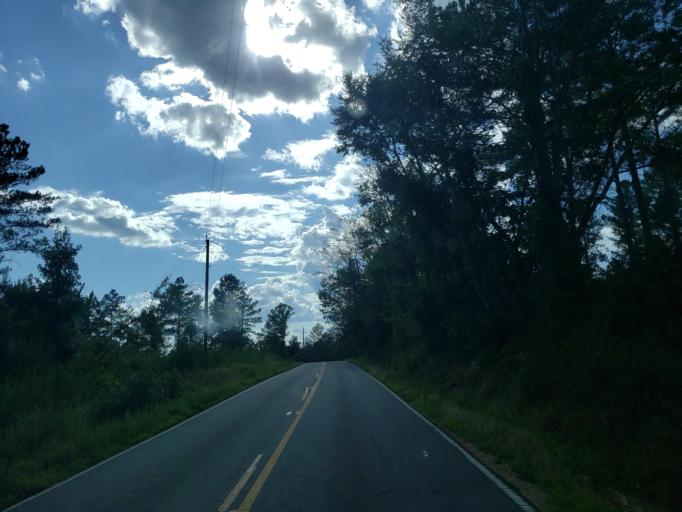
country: US
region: Georgia
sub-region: Bartow County
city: Euharlee
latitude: 34.1839
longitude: -85.0454
